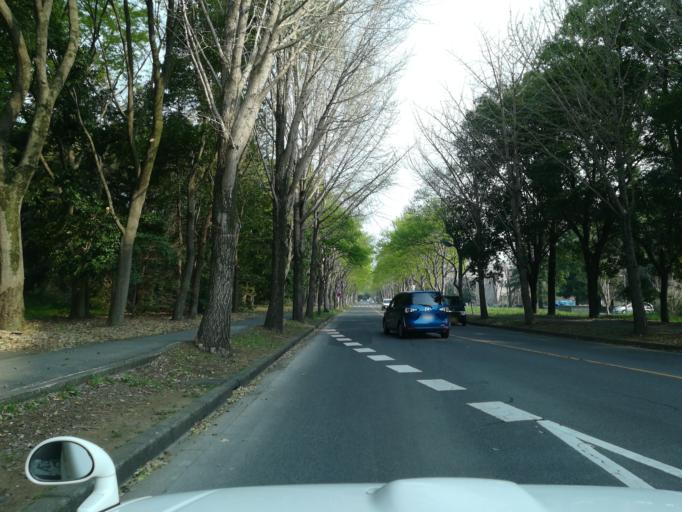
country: JP
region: Ibaraki
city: Naka
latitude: 36.1007
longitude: 140.1017
